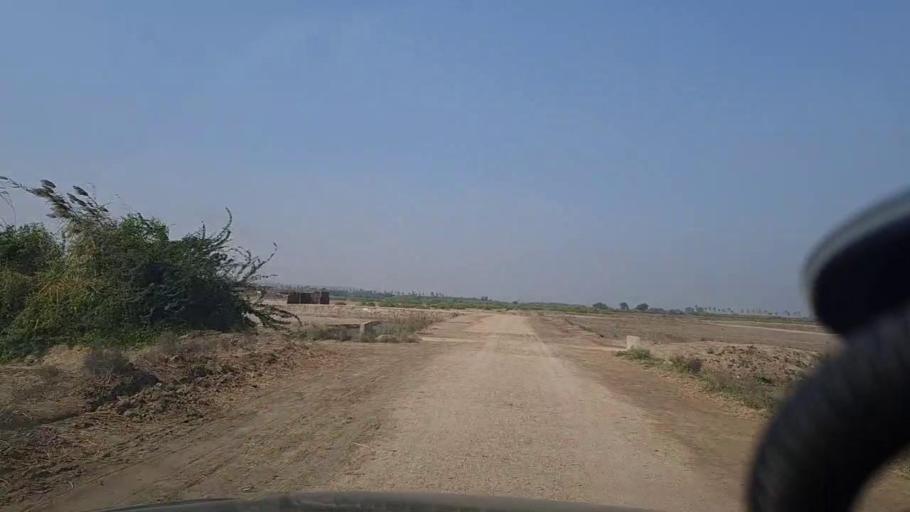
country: PK
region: Sindh
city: Thatta
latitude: 24.6188
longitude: 67.8837
